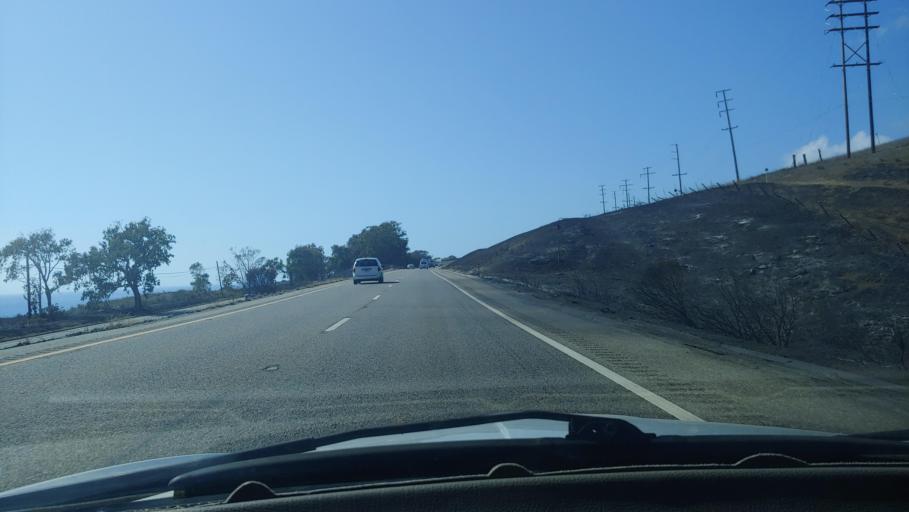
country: US
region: California
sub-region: Santa Barbara County
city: Solvang
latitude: 34.4729
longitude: -120.1613
